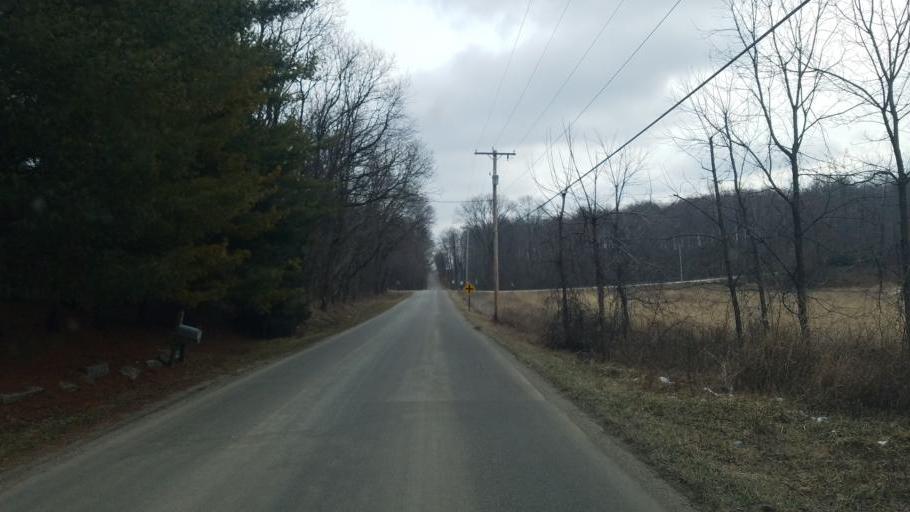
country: US
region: Ohio
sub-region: Morrow County
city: Mount Gilead
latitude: 40.5715
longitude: -82.7117
